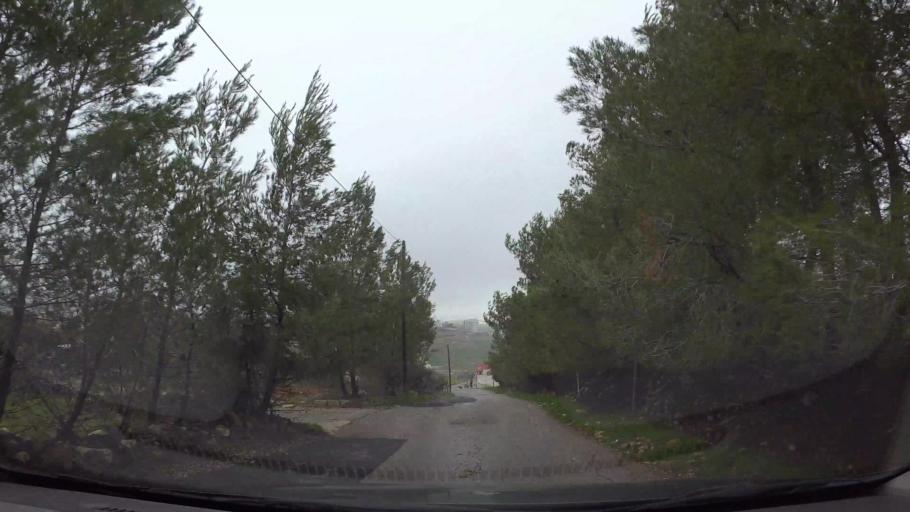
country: JO
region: Amman
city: Umm as Summaq
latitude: 31.9149
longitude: 35.8654
